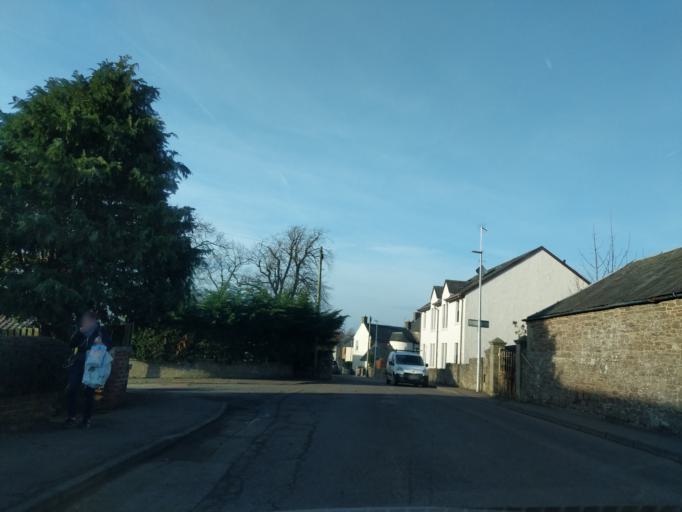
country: GB
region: Scotland
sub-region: South Lanarkshire
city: Lanark
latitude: 55.6712
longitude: -3.7759
